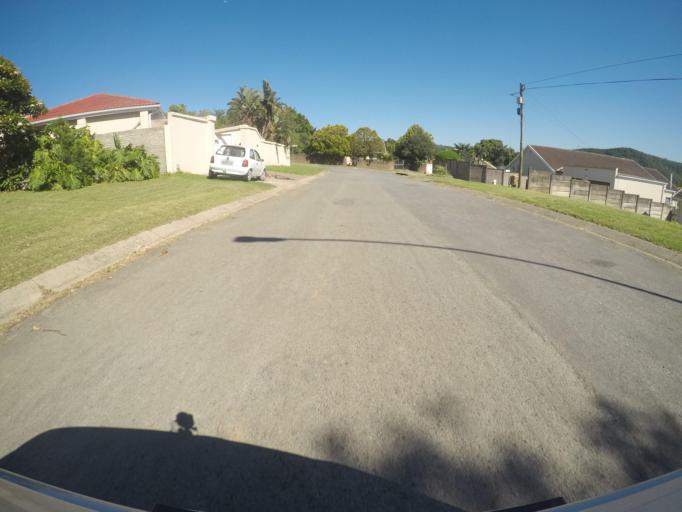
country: ZA
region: Eastern Cape
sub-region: Buffalo City Metropolitan Municipality
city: East London
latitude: -32.9472
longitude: 27.8998
